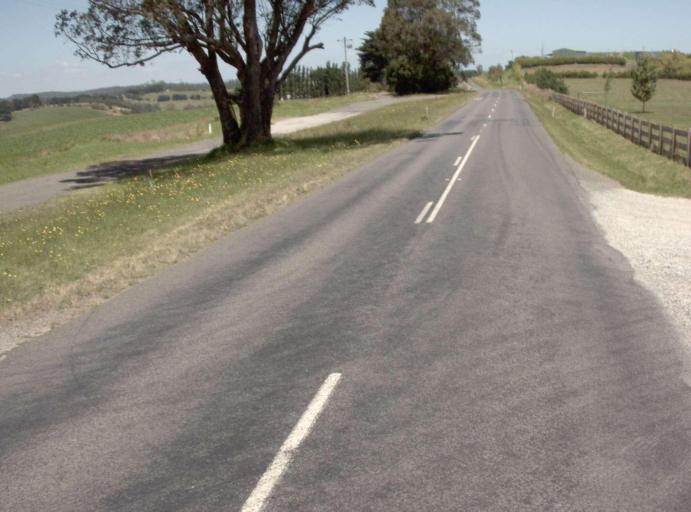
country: AU
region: Victoria
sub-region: Baw Baw
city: Warragul
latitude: -37.9956
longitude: 145.9501
